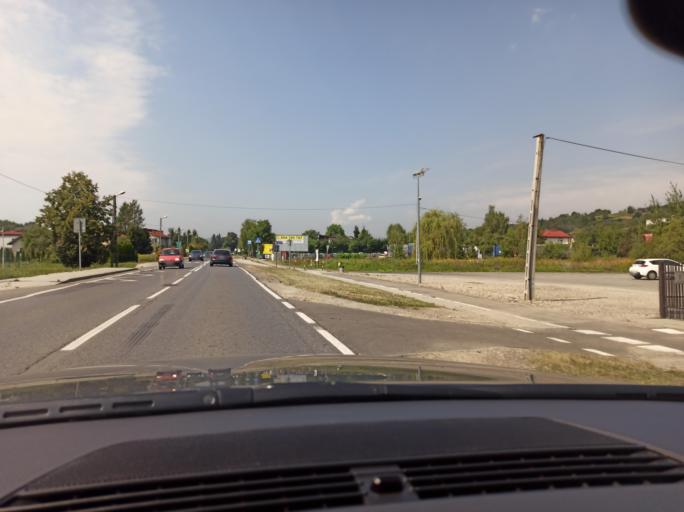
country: PL
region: Lesser Poland Voivodeship
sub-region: Powiat nowosadecki
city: Nowy Sacz
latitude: 49.6231
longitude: 20.7353
